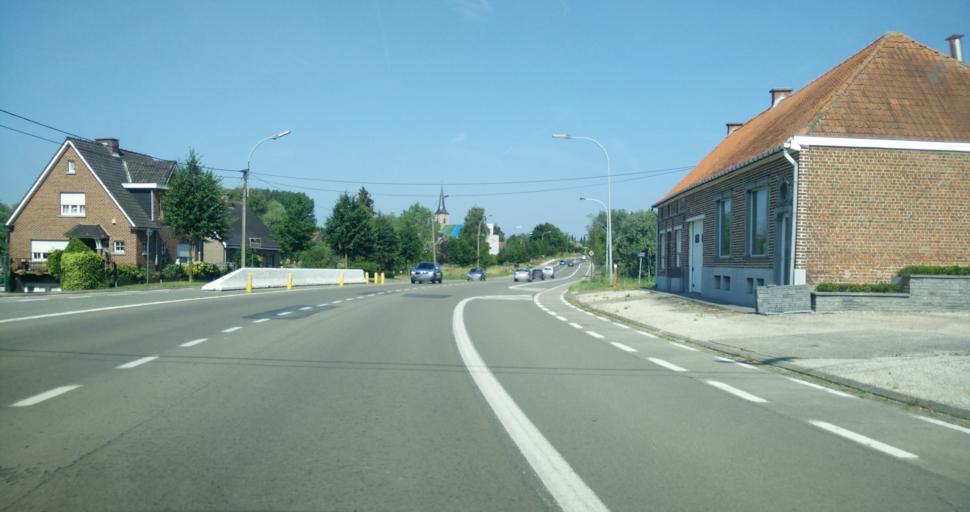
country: BE
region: Flanders
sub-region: Provincie Oost-Vlaanderen
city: Zottegem
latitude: 50.8861
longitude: 3.7601
